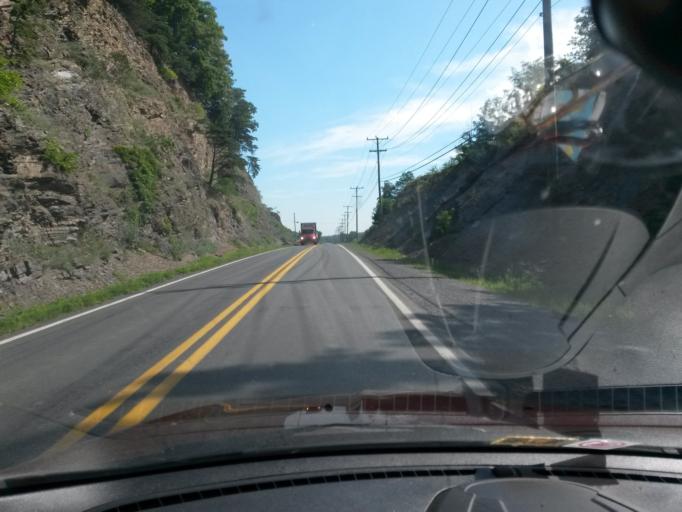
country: US
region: Virginia
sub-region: Shenandoah County
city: Basye
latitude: 38.8856
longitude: -78.8616
